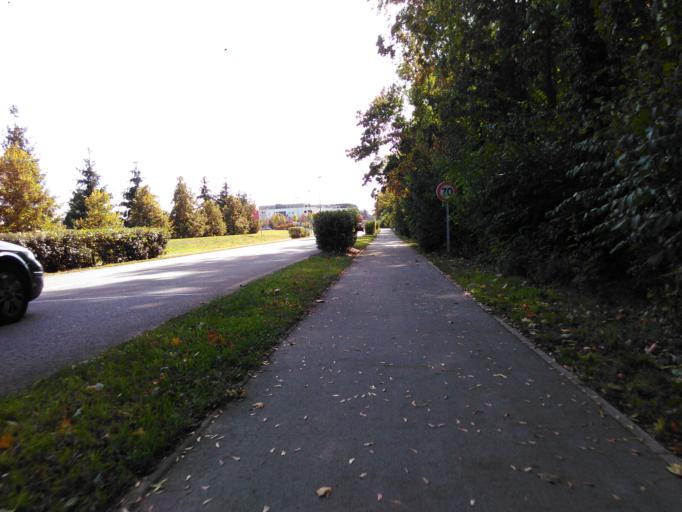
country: FR
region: Lorraine
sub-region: Departement de la Moselle
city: Thionville
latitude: 49.3803
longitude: 6.1693
